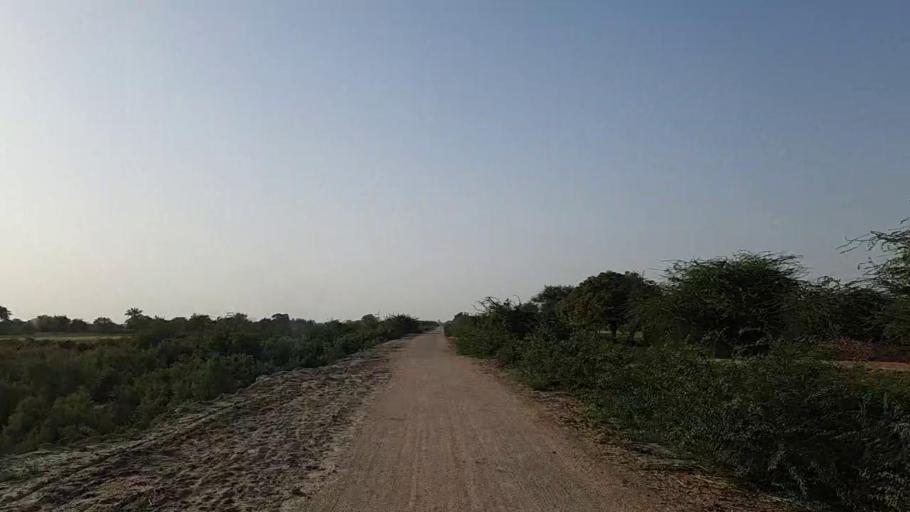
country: PK
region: Sindh
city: Jati
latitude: 24.3335
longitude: 68.1558
